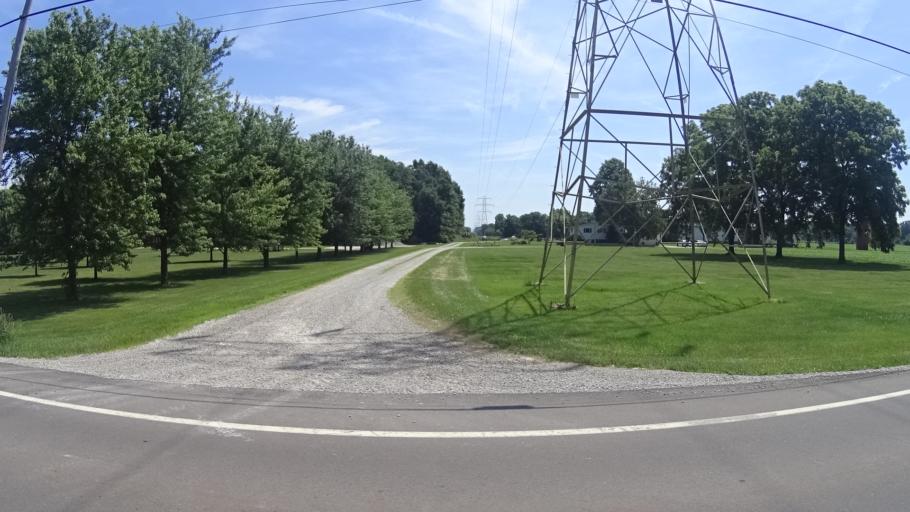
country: US
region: Ohio
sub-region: Erie County
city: Huron
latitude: 41.3576
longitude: -82.4942
